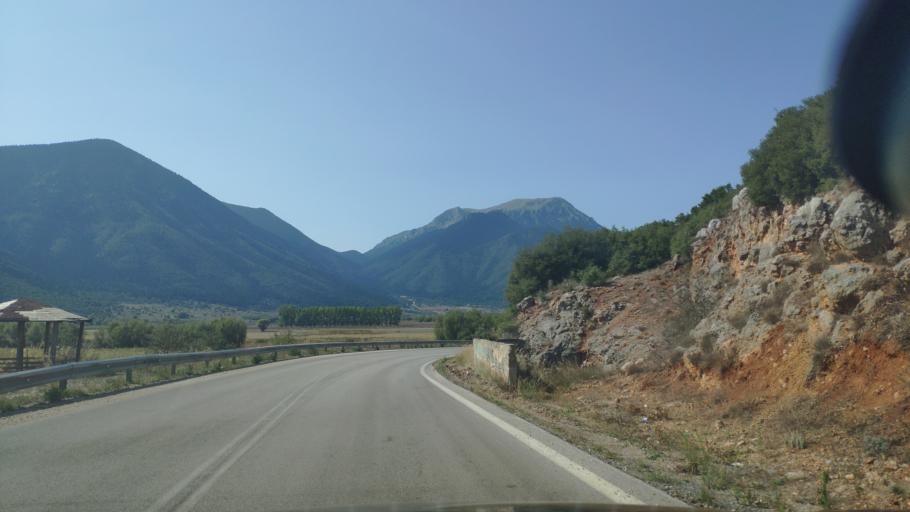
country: GR
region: Peloponnese
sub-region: Nomos Korinthias
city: Nemea
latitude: 37.8542
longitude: 22.4504
